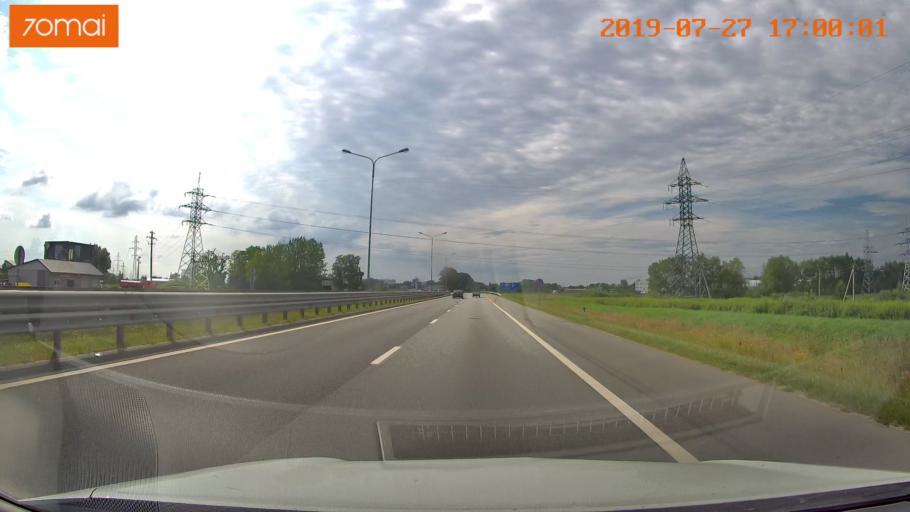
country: RU
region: Kaliningrad
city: Bol'shoe Isakovo
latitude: 54.7065
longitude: 20.6351
